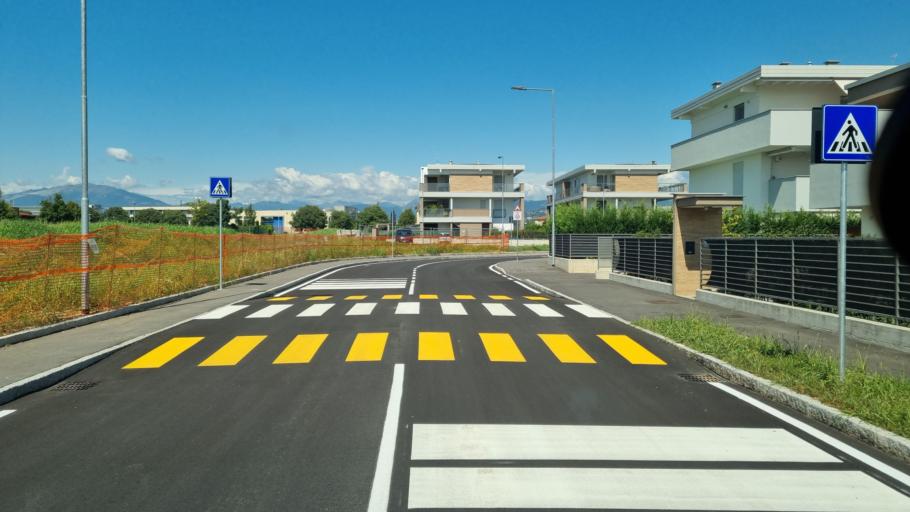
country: IT
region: Lombardy
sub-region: Provincia di Bergamo
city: Stezzano
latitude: 45.6451
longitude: 9.6436
